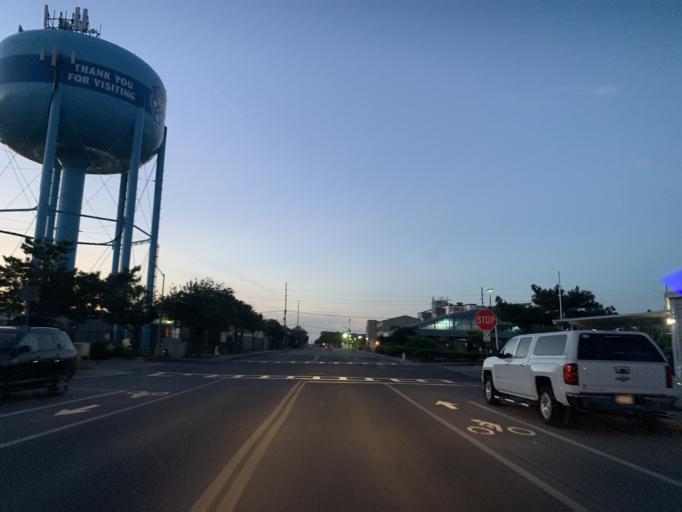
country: US
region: Delaware
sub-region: Sussex County
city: Bethany Beach
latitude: 38.4413
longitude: -75.0549
